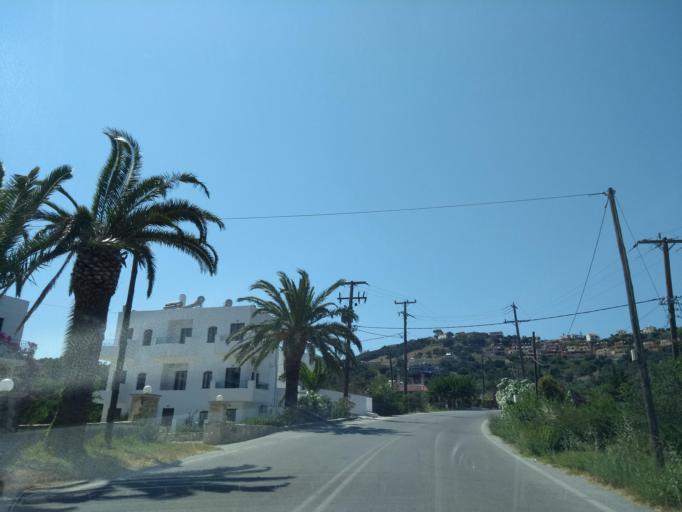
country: GR
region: Crete
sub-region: Nomos Chanias
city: Georgioupolis
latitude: 35.3693
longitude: 24.2479
